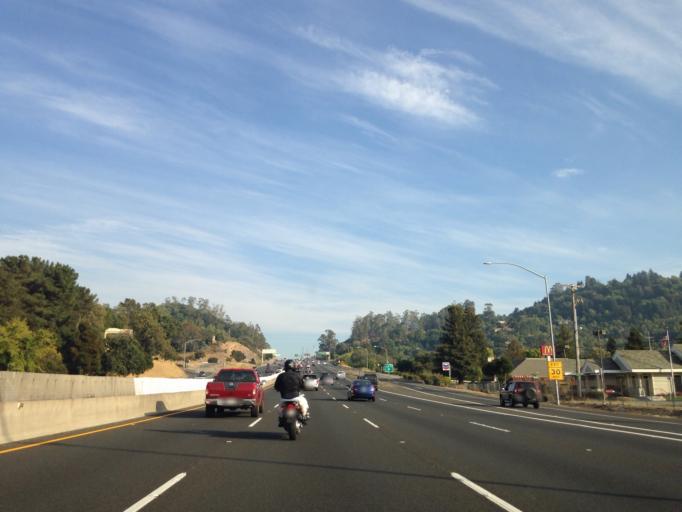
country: US
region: California
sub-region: Marin County
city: Santa Venetia
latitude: 37.9974
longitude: -122.5347
